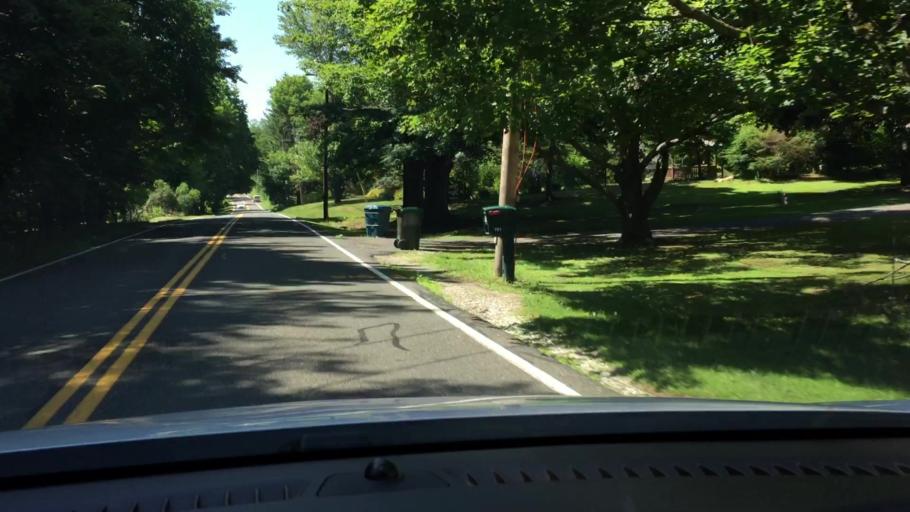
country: US
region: Massachusetts
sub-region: Berkshire County
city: Lenox
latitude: 42.3903
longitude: -73.2558
